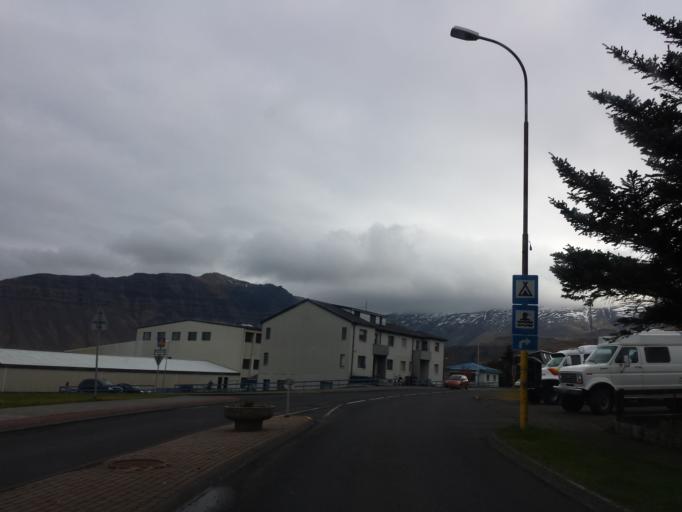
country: IS
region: West
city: Olafsvik
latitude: 64.9247
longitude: -23.2582
